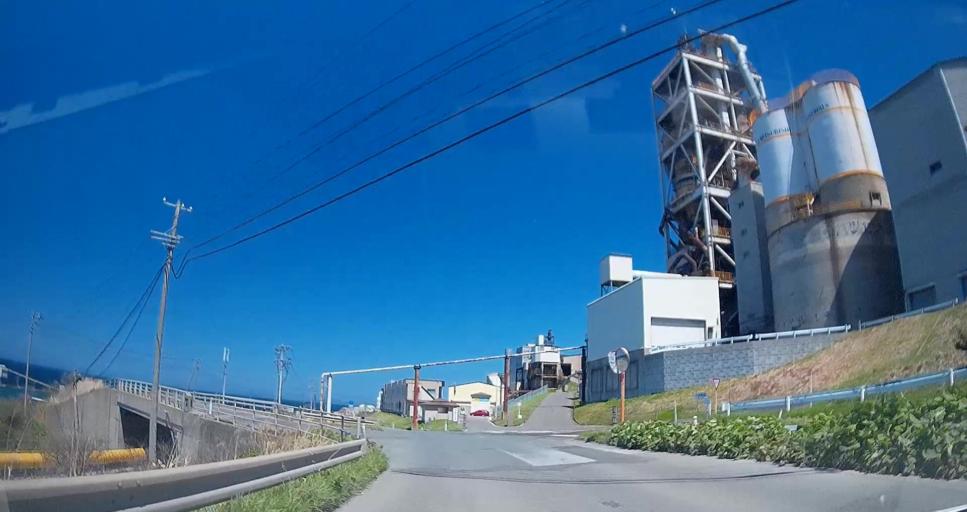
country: JP
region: Aomori
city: Mutsu
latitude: 41.4061
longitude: 141.4354
